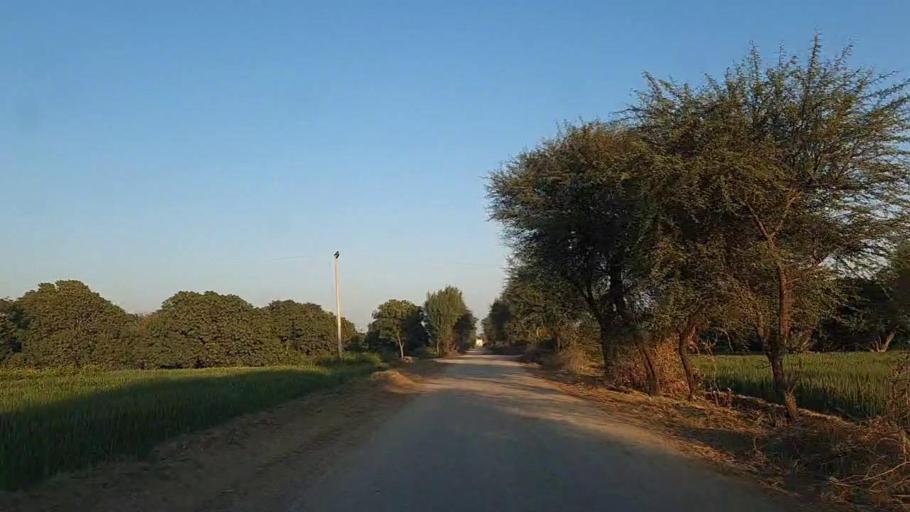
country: PK
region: Sindh
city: Naukot
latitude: 25.0329
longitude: 69.4222
